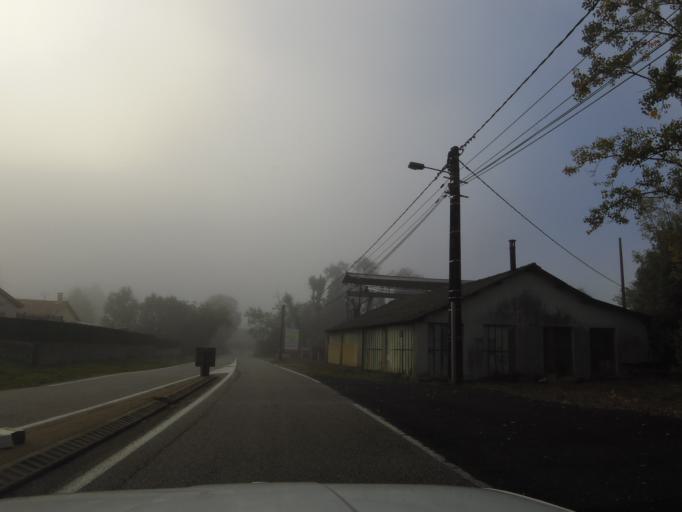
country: FR
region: Rhone-Alpes
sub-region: Departement de l'Ain
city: Villebois
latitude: 45.8430
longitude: 5.4219
